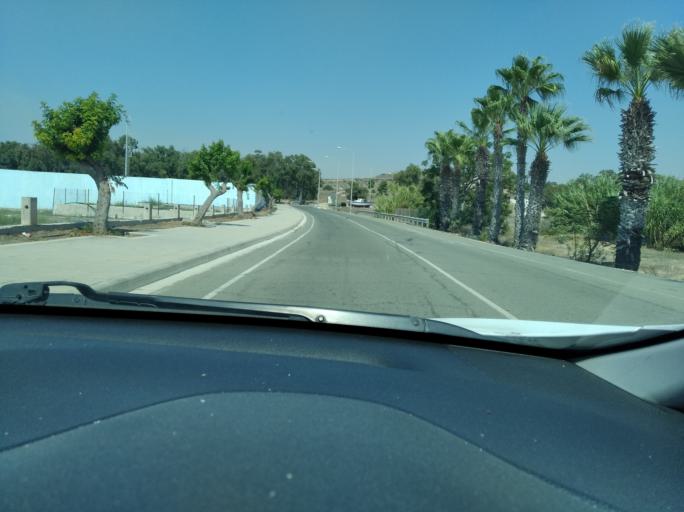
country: CY
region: Larnaka
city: Xylotymbou
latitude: 34.9839
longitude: 33.7804
